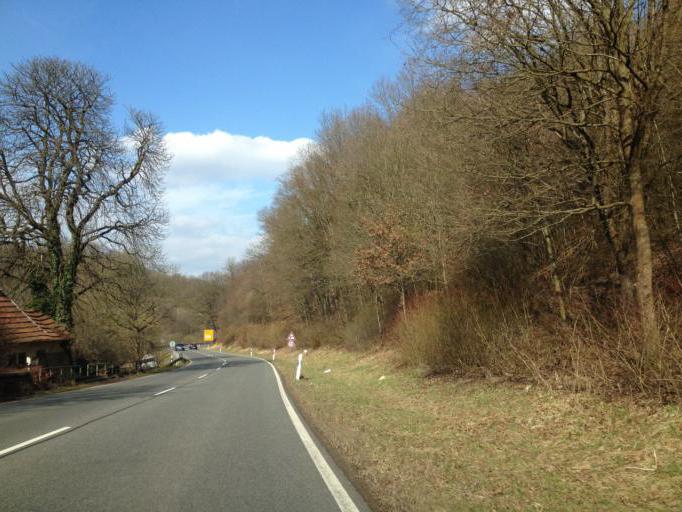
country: DE
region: Saarland
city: Sankt Wendel
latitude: 49.4435
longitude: 7.1469
